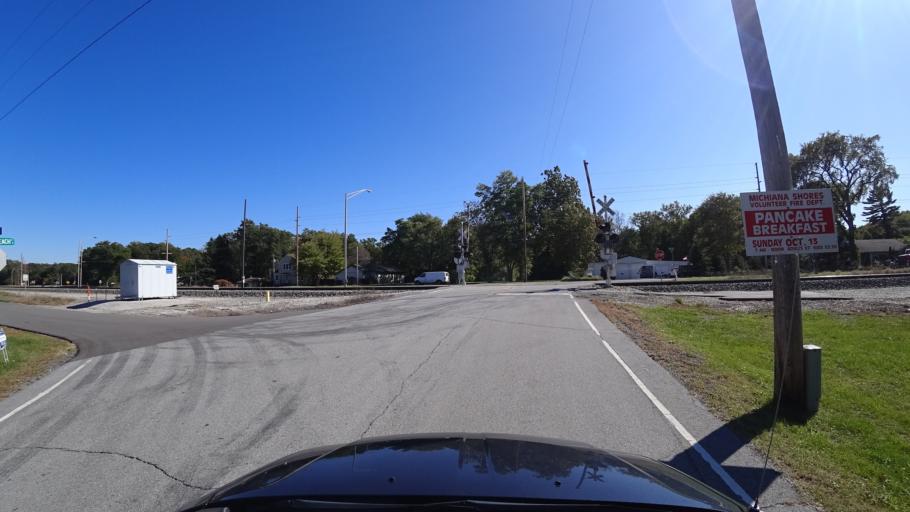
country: US
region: Indiana
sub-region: LaPorte County
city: Long Beach
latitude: 41.7444
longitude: -86.8310
